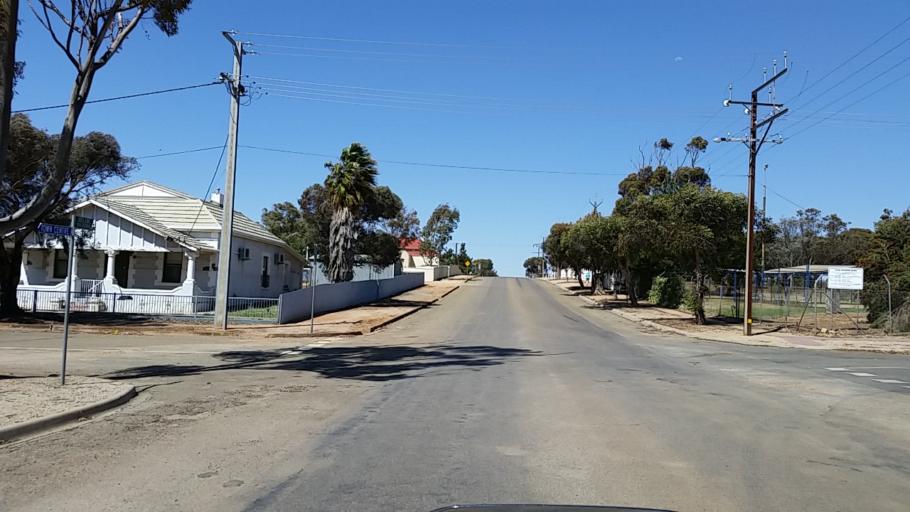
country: AU
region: South Australia
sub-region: Peterborough
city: Peterborough
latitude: -32.9784
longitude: 138.8325
